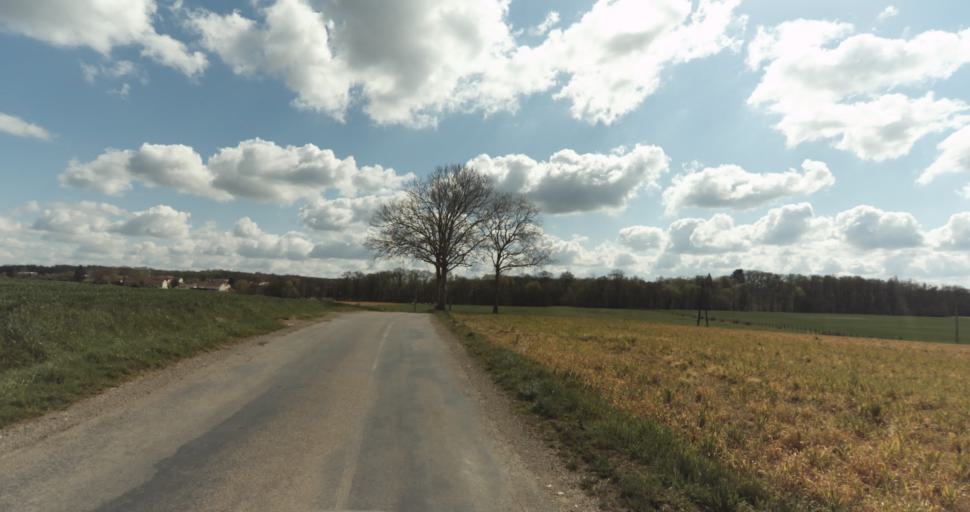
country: FR
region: Bourgogne
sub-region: Departement de la Cote-d'Or
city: Auxonne
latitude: 47.2068
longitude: 5.4233
